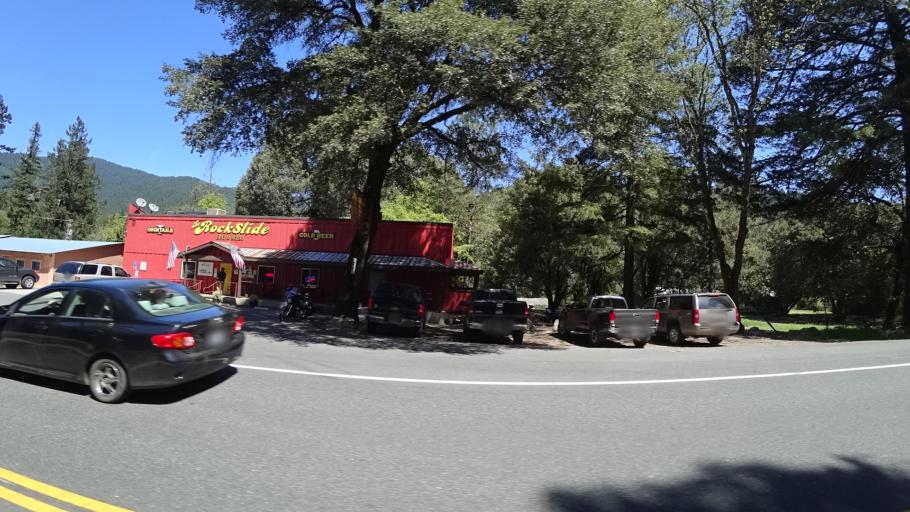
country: US
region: California
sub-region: Humboldt County
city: Willow Creek
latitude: 40.8696
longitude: -123.5220
